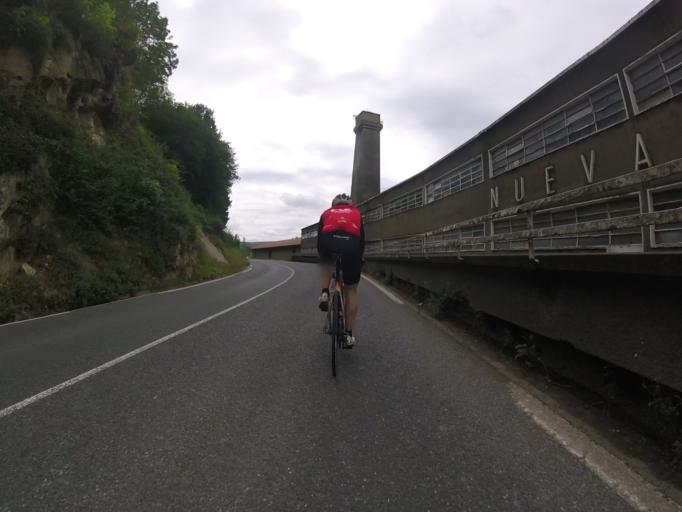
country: ES
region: Basque Country
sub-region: Provincia de Guipuzcoa
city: Orio
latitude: 43.2766
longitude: -2.1217
